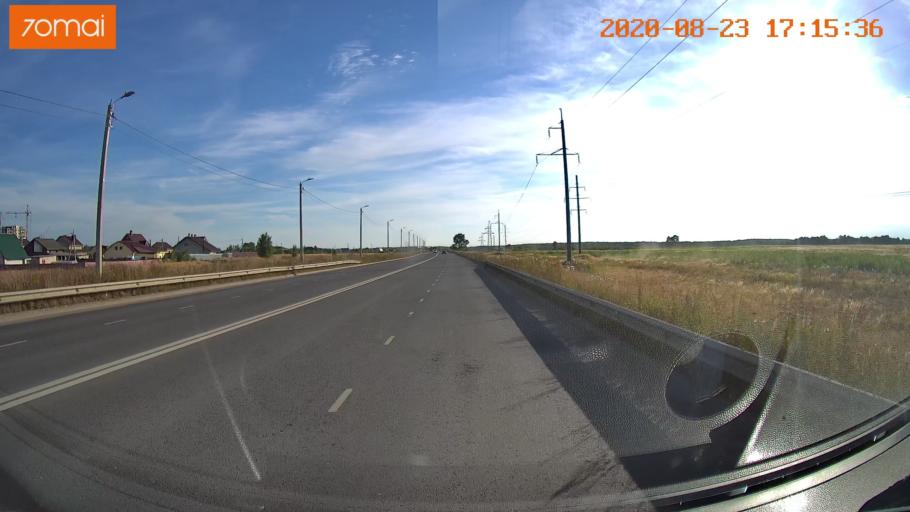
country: RU
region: Ivanovo
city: Novo-Talitsy
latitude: 57.0444
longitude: 40.9109
